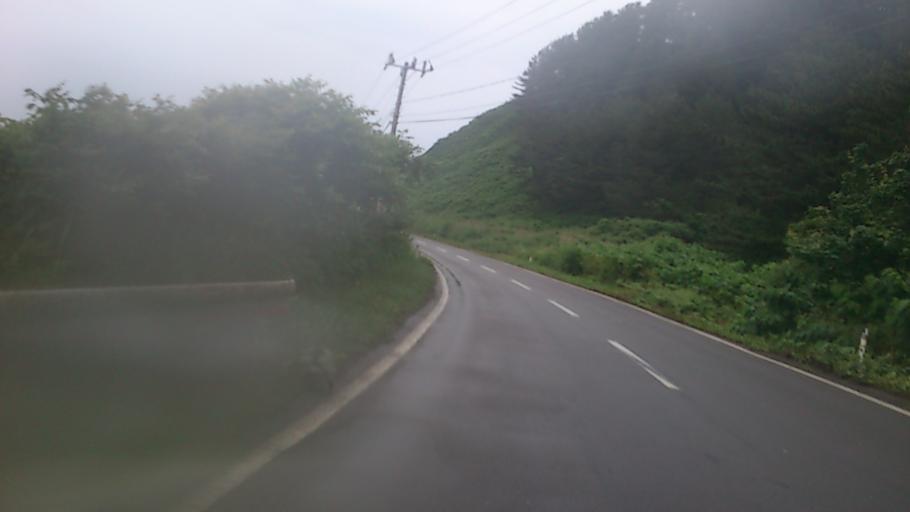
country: JP
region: Akita
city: Noshiromachi
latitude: 40.4652
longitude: 139.9465
